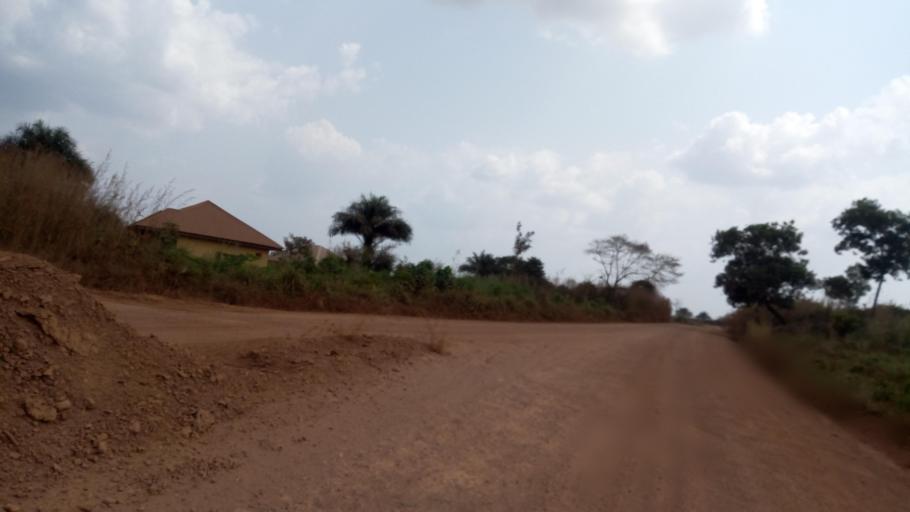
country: SL
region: Southern Province
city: Mogbwemo
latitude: 7.7864
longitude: -12.3137
